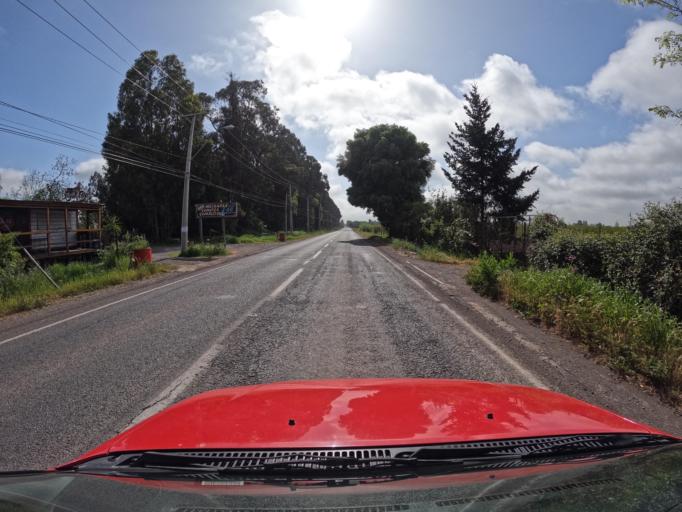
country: CL
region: Maule
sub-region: Provincia de Curico
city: Teno
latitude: -34.8668
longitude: -71.2096
